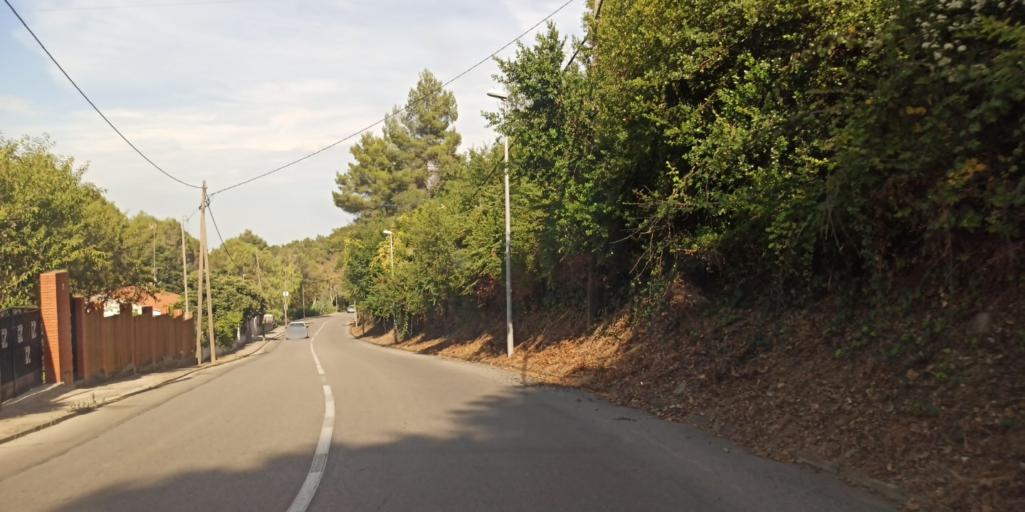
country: ES
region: Catalonia
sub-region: Provincia de Barcelona
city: Santa Coloma de Cervello
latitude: 41.3613
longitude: 2.0055
